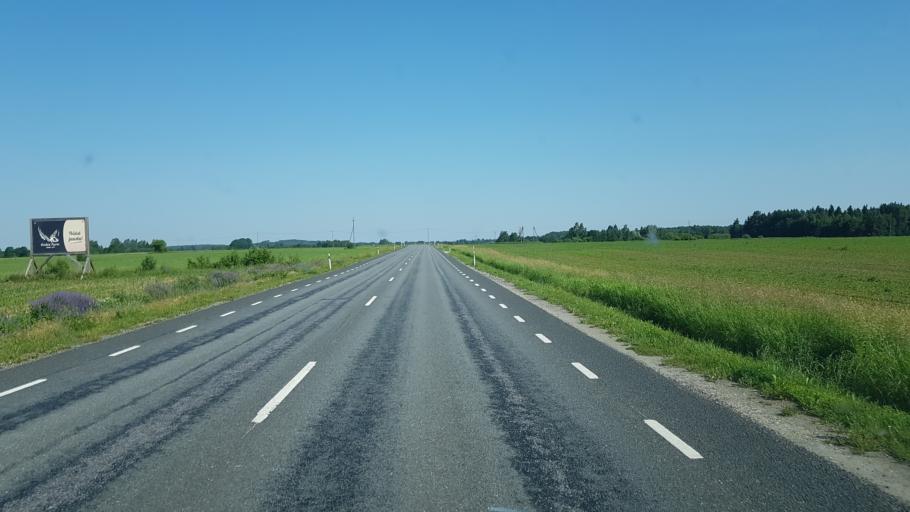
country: EE
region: Tartu
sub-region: UElenurme vald
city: Ulenurme
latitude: 58.1922
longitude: 26.8203
